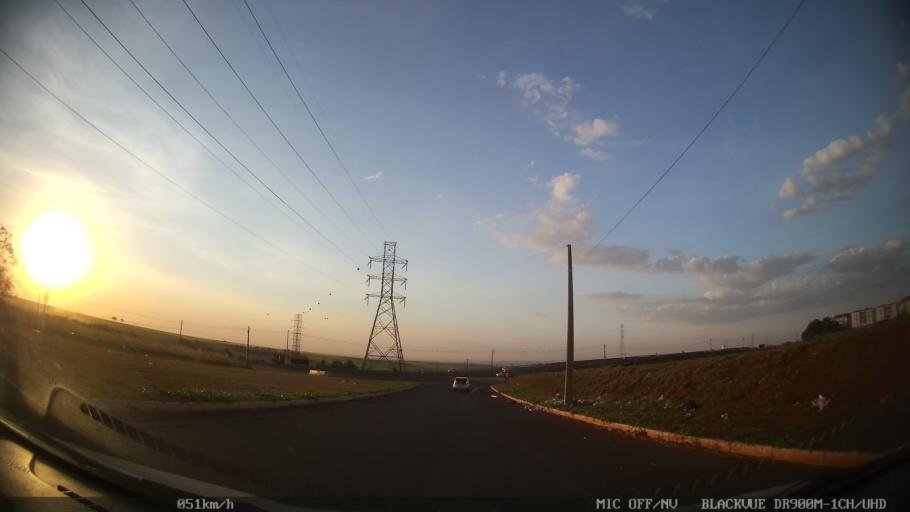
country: BR
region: Sao Paulo
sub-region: Ribeirao Preto
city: Ribeirao Preto
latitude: -21.1365
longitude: -47.8575
